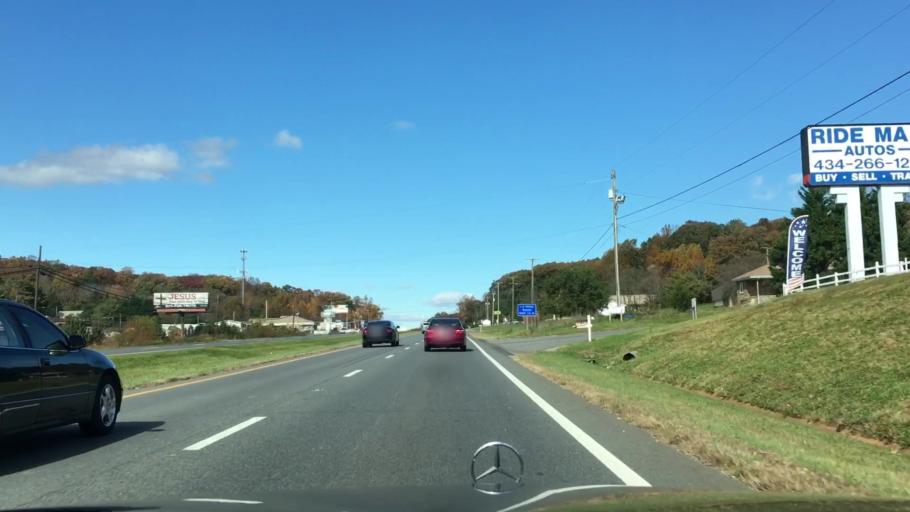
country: US
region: Virginia
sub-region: Campbell County
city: Rustburg
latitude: 37.2942
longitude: -79.1706
